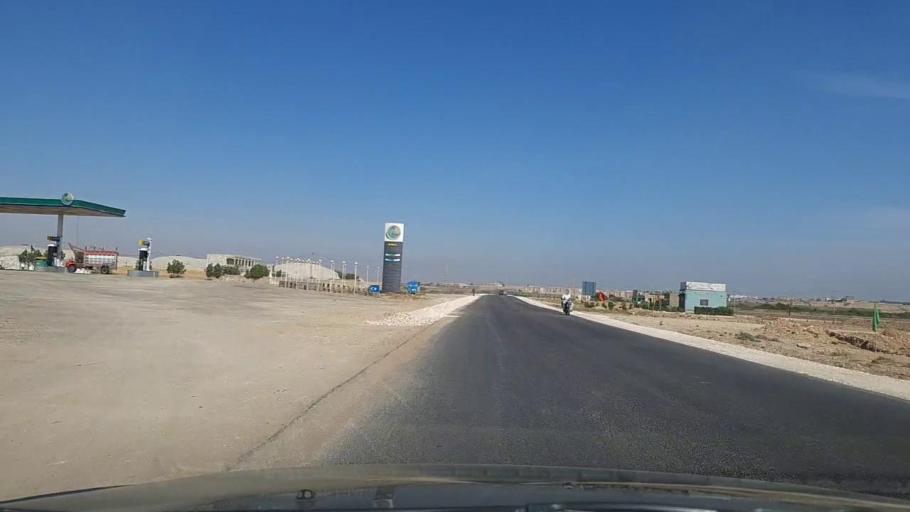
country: PK
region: Sindh
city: Kotri
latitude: 25.3246
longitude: 68.2361
